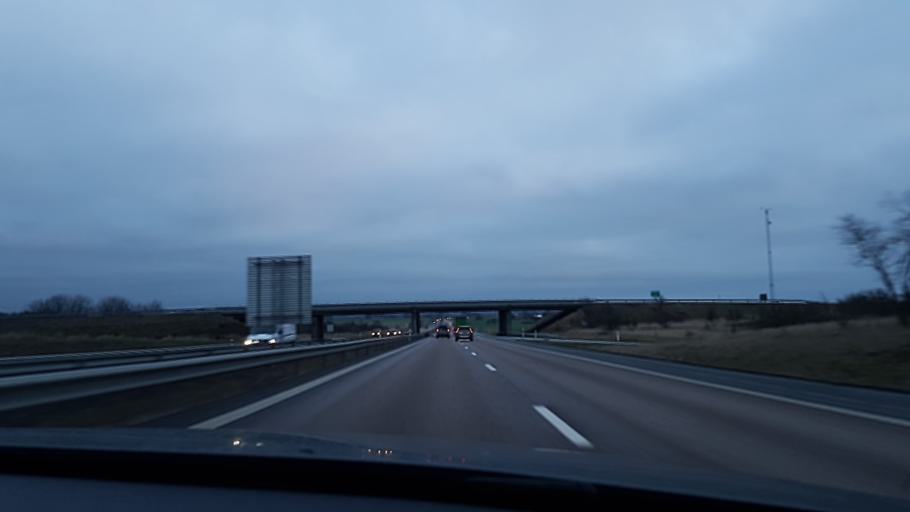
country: SE
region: Skane
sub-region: Helsingborg
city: Glumslov
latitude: 55.9251
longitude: 12.8352
